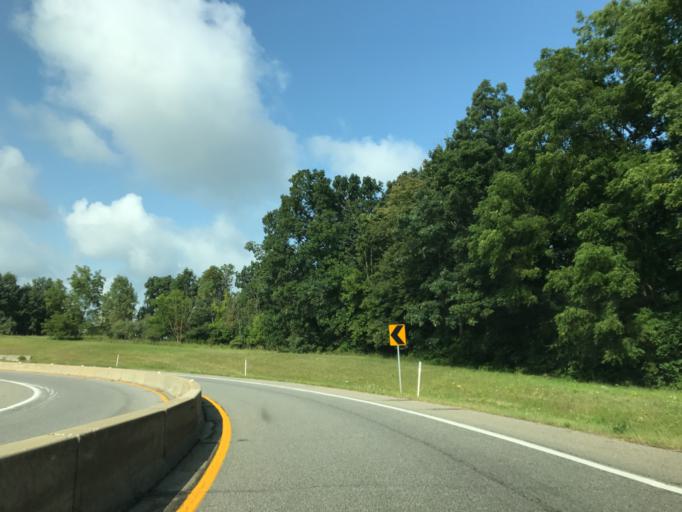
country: US
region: Indiana
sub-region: Steuben County
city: Fremont
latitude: 41.7371
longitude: -84.9933
